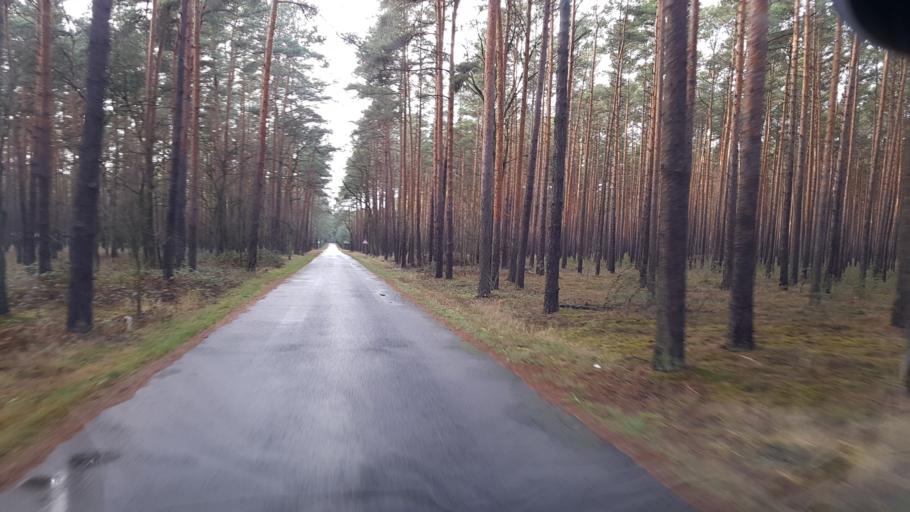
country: DE
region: Brandenburg
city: Bronkow
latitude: 51.6692
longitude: 13.8970
